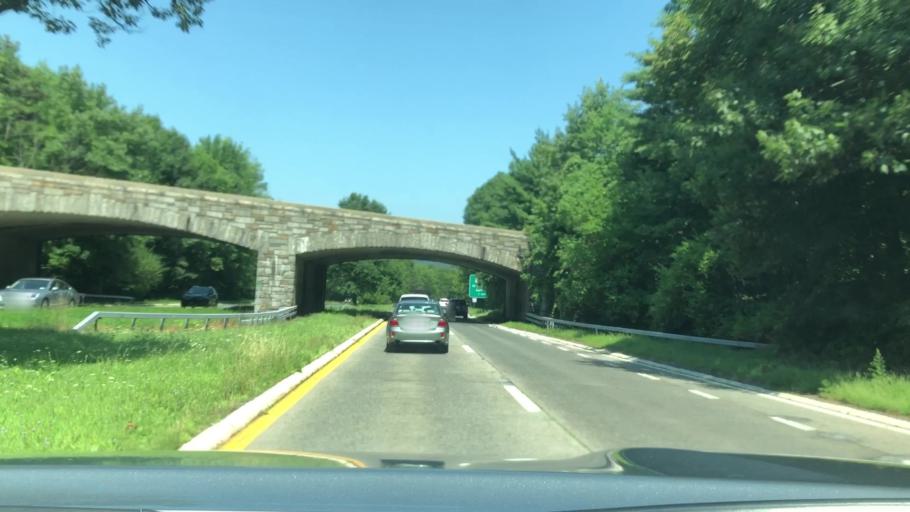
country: US
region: New York
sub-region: Rockland County
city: Pomona
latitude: 41.1716
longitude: -74.0323
